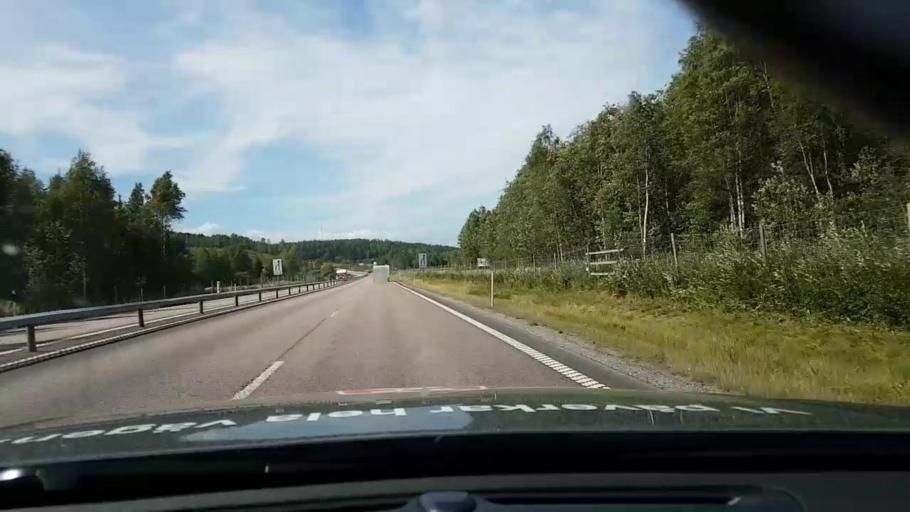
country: SE
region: Vaesternorrland
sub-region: OErnskoeldsviks Kommun
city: Ornskoldsvik
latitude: 63.3059
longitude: 18.8506
